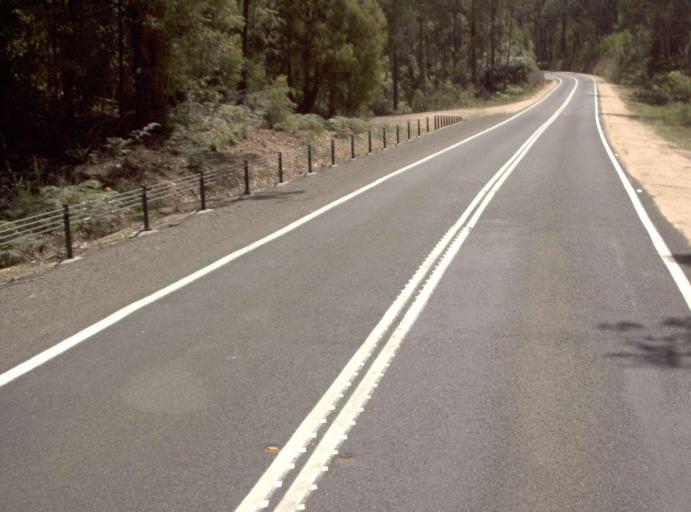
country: AU
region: New South Wales
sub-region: Bombala
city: Bombala
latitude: -37.5844
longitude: 148.9997
